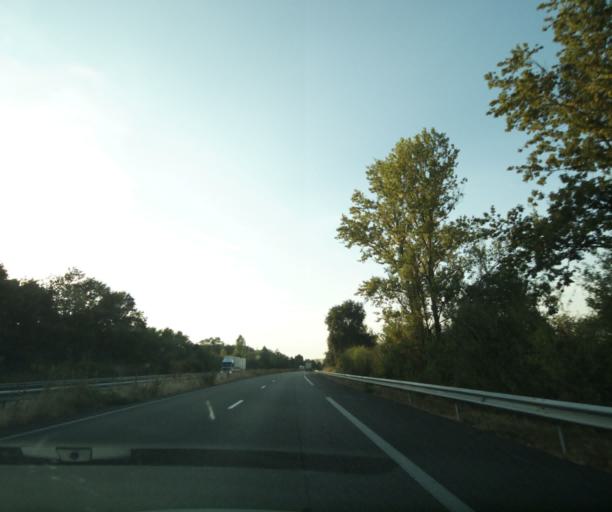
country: FR
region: Aquitaine
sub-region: Departement du Lot-et-Garonne
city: Layrac
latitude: 44.1118
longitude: 0.7315
